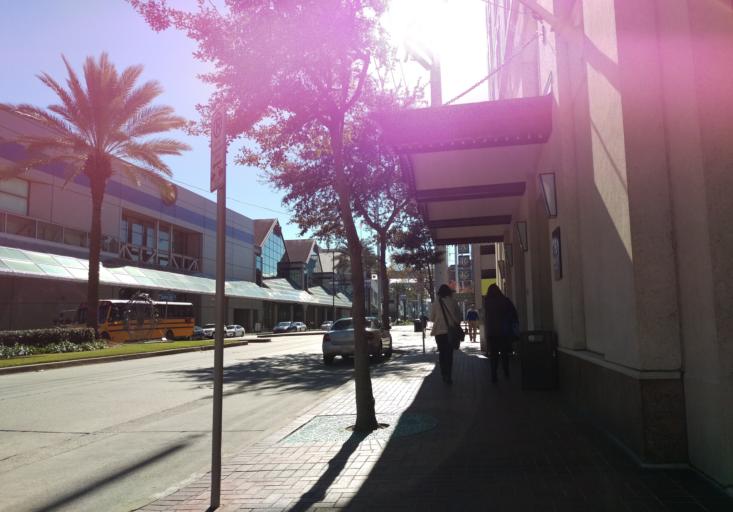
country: US
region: Louisiana
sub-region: Orleans Parish
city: New Orleans
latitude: 29.9426
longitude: -90.0647
